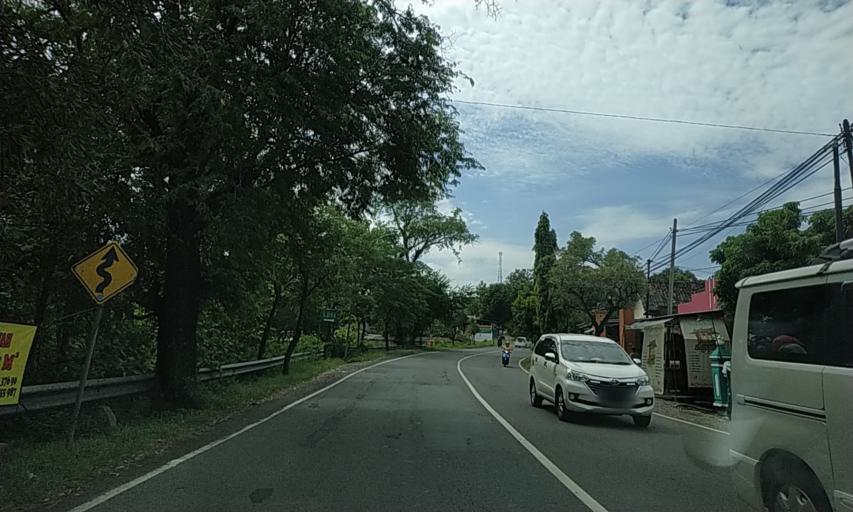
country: ID
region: Central Java
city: Selogiri
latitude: -7.7938
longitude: 110.9005
